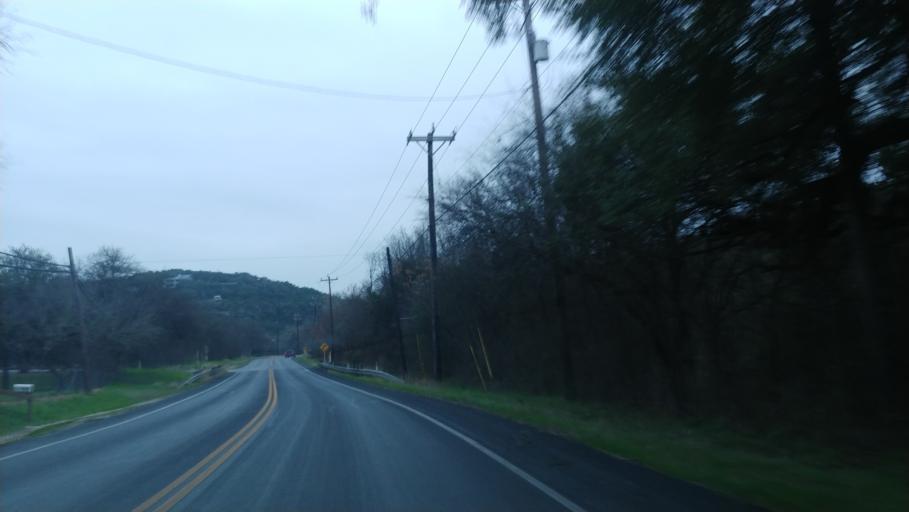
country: US
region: Texas
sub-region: Bexar County
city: Helotes
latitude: 29.5870
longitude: -98.6883
